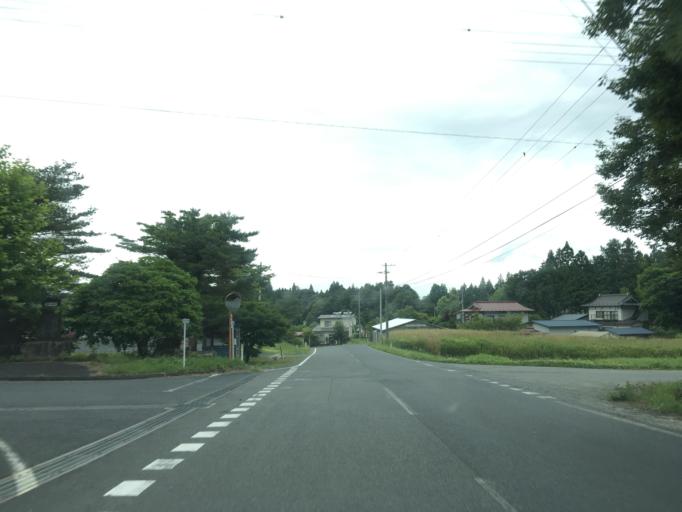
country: JP
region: Iwate
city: Ichinoseki
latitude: 38.8359
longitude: 141.3501
